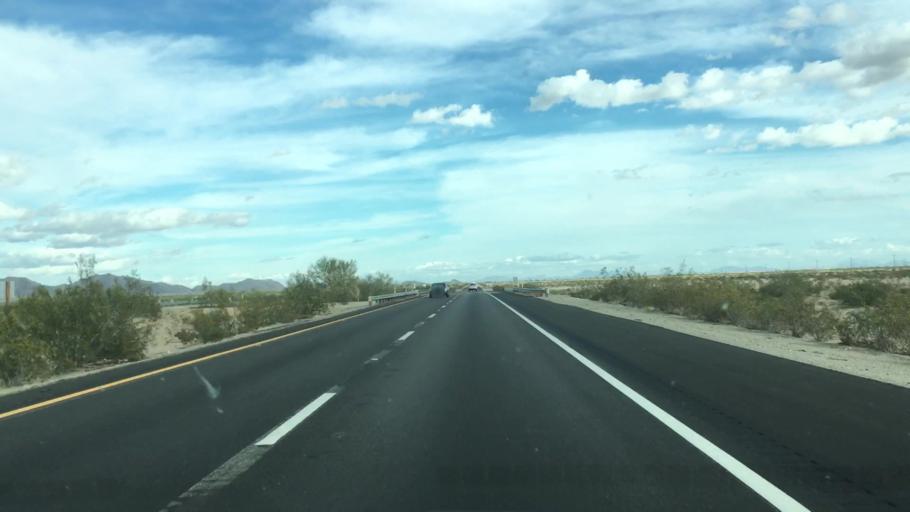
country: US
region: California
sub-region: Riverside County
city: Mesa Verde
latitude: 33.6082
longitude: -114.8838
